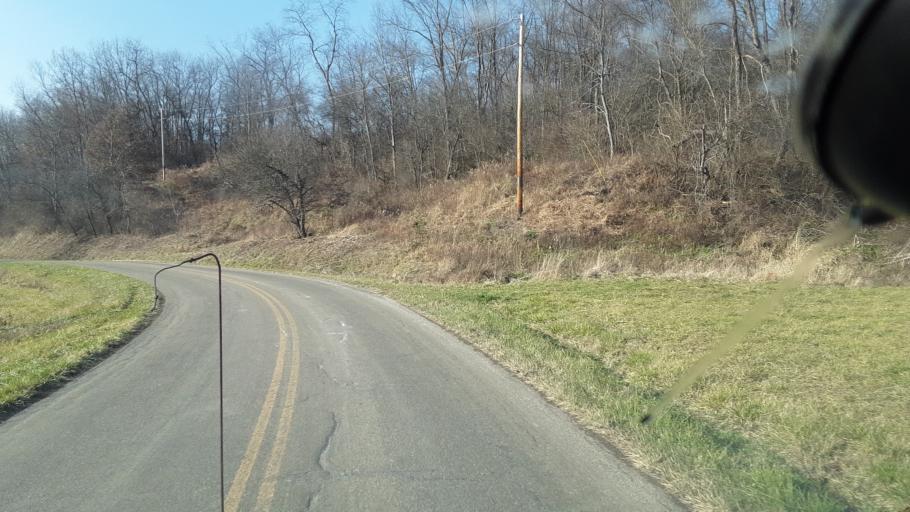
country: US
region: Ohio
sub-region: Knox County
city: Oak Hill
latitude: 40.4115
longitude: -82.2069
